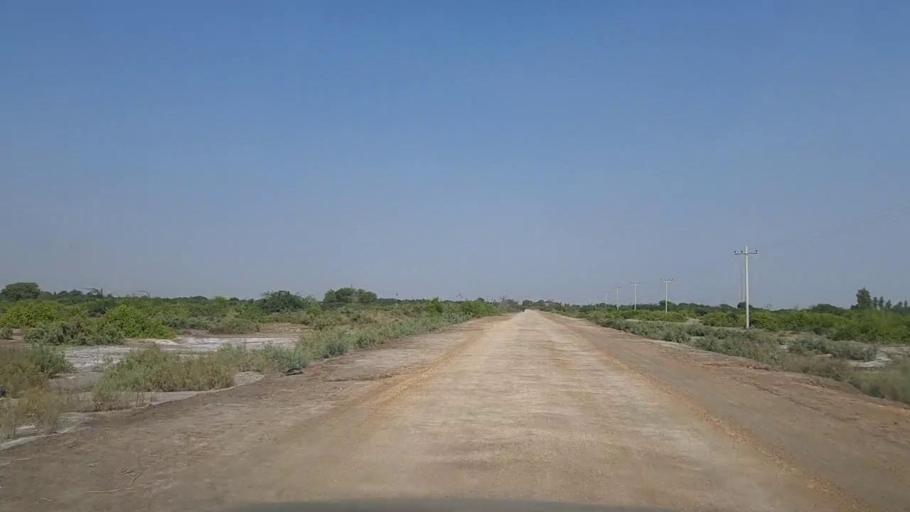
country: PK
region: Sindh
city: Thatta
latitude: 24.6081
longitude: 67.9556
